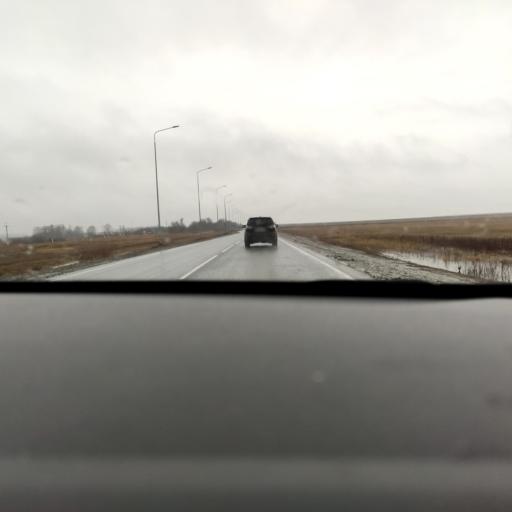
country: RU
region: Tatarstan
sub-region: Alekseyevskiy Rayon
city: Alekseyevskoye
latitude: 55.3128
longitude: 50.2920
